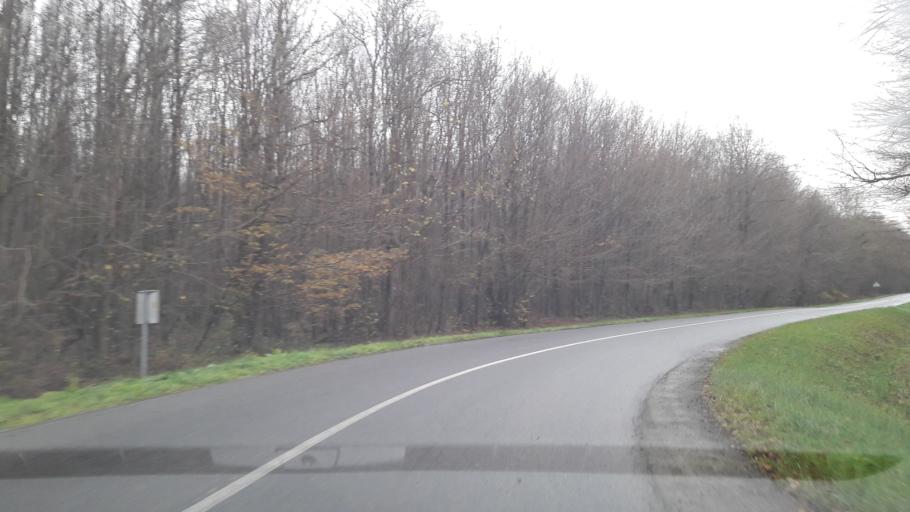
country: HR
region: Osjecko-Baranjska
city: Velimirovac
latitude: 45.6296
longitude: 18.0884
